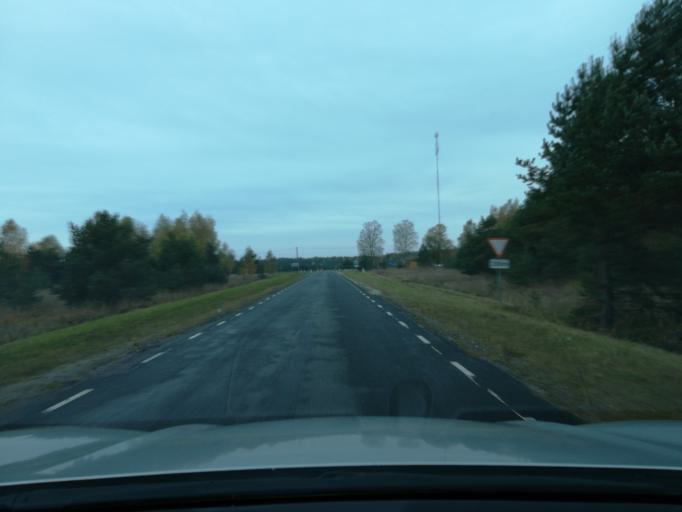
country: EE
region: Jogevamaa
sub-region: Mustvee linn
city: Mustvee
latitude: 58.9981
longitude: 27.2297
